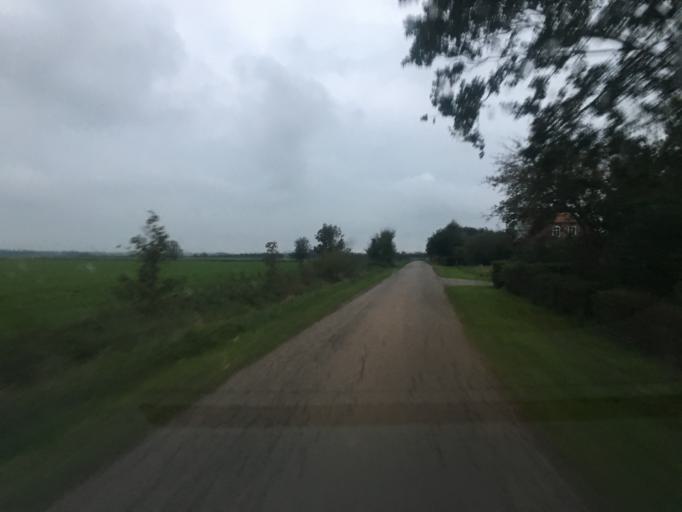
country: DK
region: South Denmark
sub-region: Tonder Kommune
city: Sherrebek
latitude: 55.0395
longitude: 8.8012
